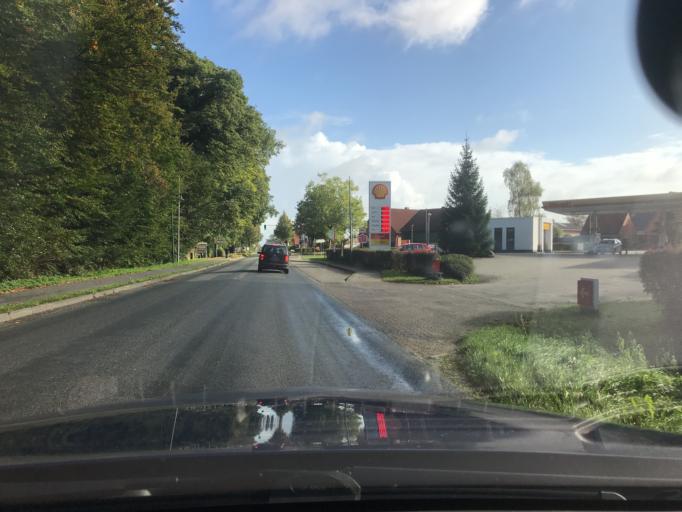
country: DE
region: Lower Saxony
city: Harsefeld
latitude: 53.4487
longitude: 9.4914
